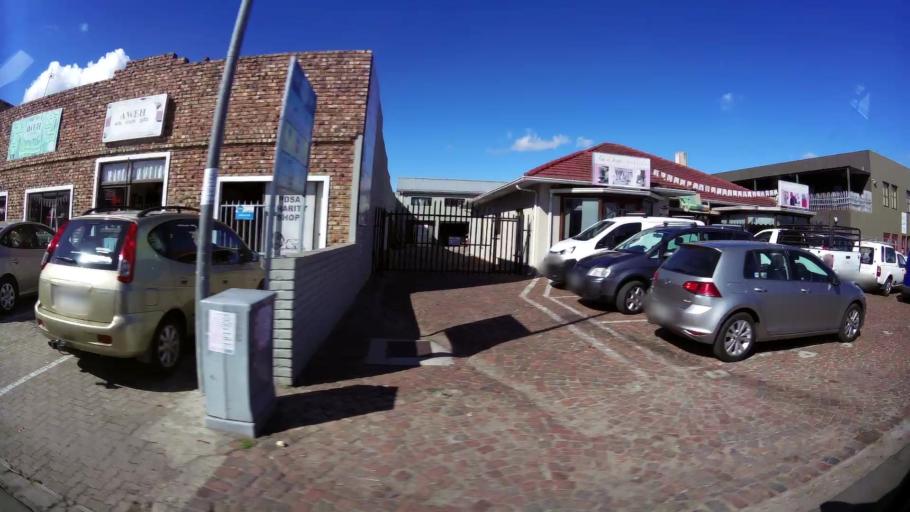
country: ZA
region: Western Cape
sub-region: Eden District Municipality
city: George
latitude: -33.9577
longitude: 22.4649
